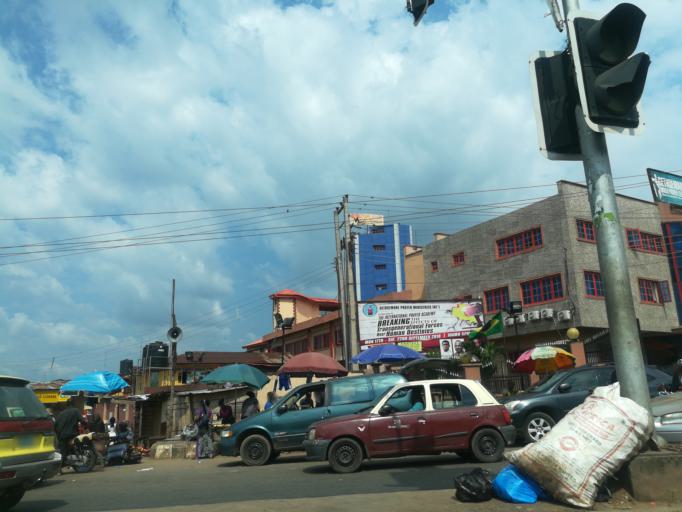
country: NG
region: Oyo
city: Ibadan
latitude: 7.4193
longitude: 3.8595
